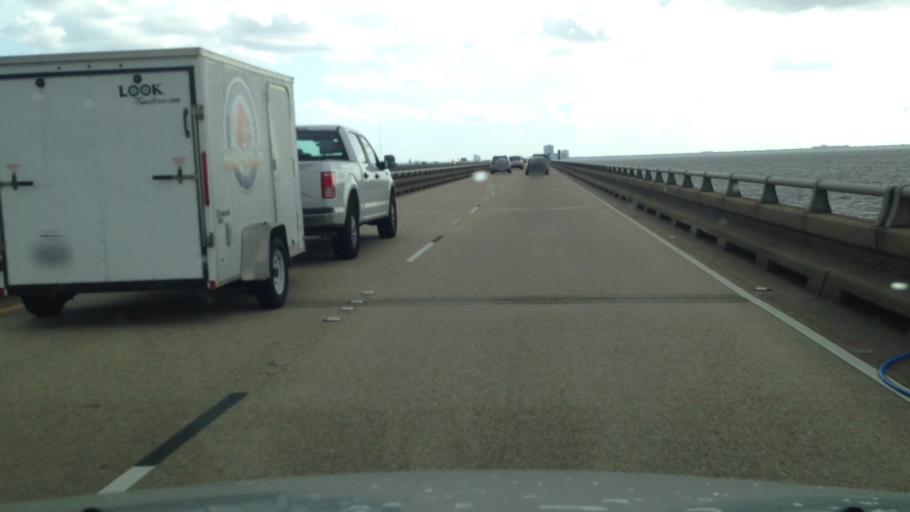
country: US
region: Louisiana
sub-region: Jefferson Parish
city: Metairie
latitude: 30.0877
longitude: -90.1426
